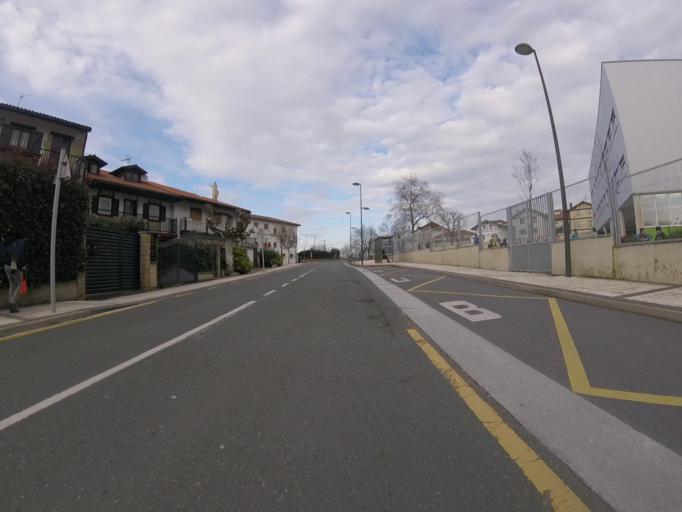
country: ES
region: Basque Country
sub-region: Provincia de Guipuzcoa
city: Irun
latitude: 43.3279
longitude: -1.8198
